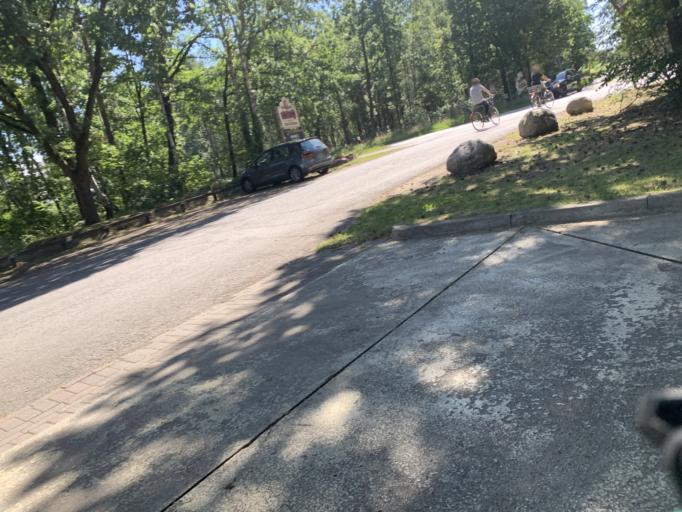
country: DE
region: Lower Saxony
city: Wietzendorf
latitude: 52.9328
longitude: 9.9717
